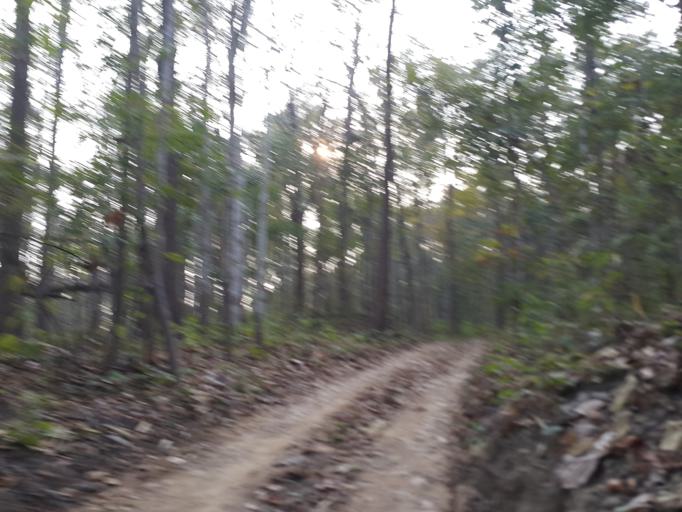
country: TH
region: Lamphun
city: Li
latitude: 17.6162
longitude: 98.8958
